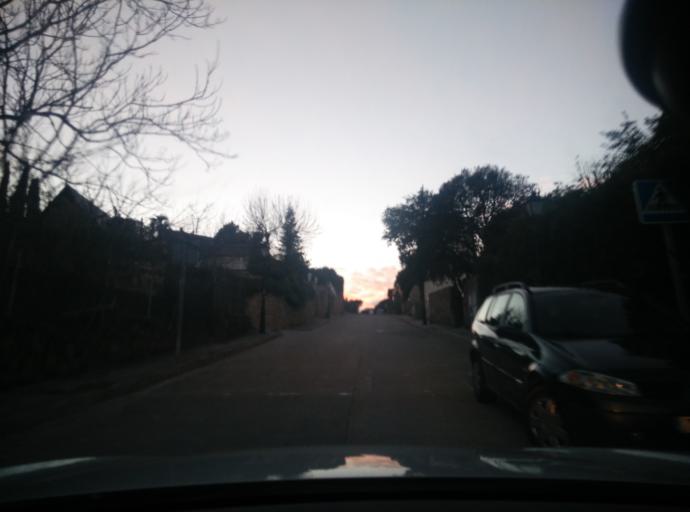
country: ES
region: Madrid
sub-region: Provincia de Madrid
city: Manzanares el Real
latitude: 40.7346
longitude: -3.8503
